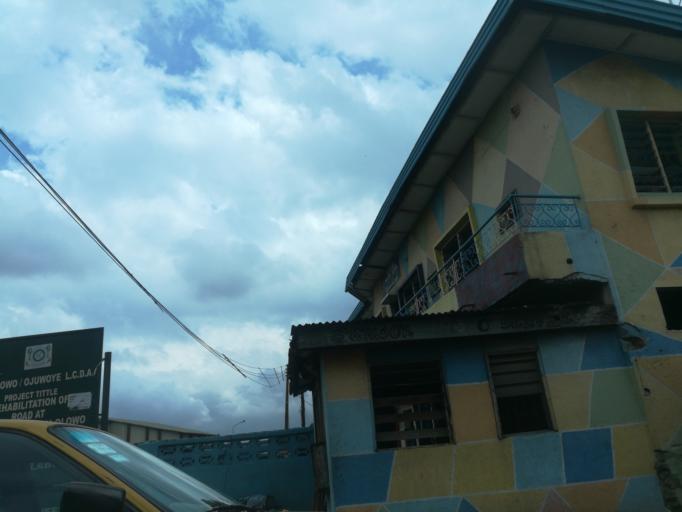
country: NG
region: Lagos
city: Mushin
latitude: 6.5324
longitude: 3.3583
